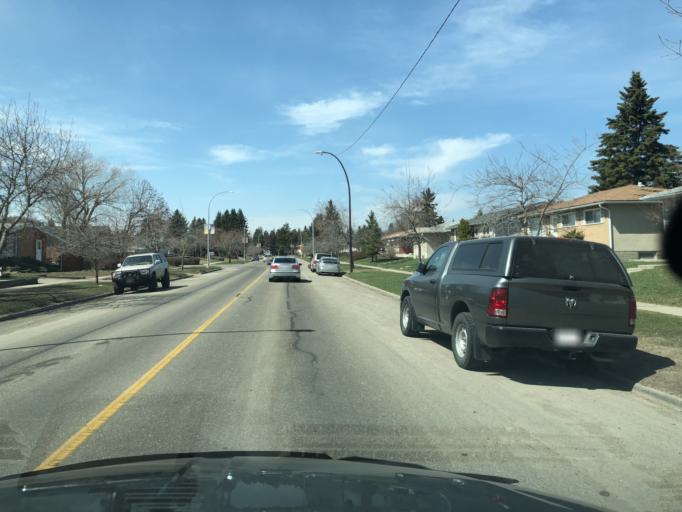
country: CA
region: Alberta
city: Calgary
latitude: 50.9707
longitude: -114.0505
